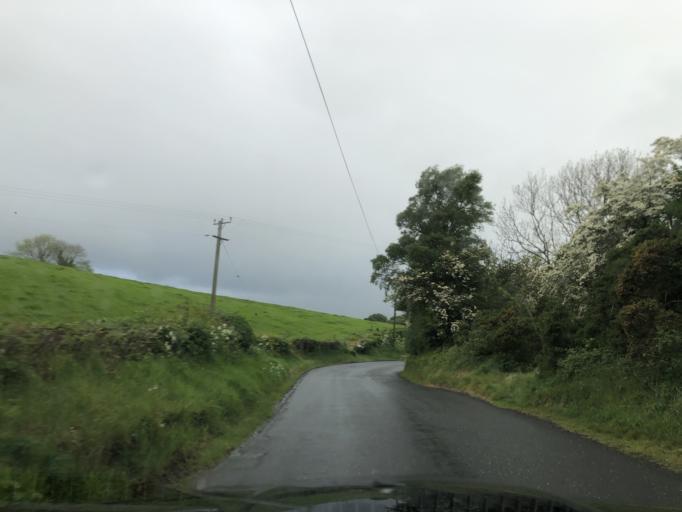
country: GB
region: Northern Ireland
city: Dunloy
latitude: 55.1356
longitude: -6.3696
